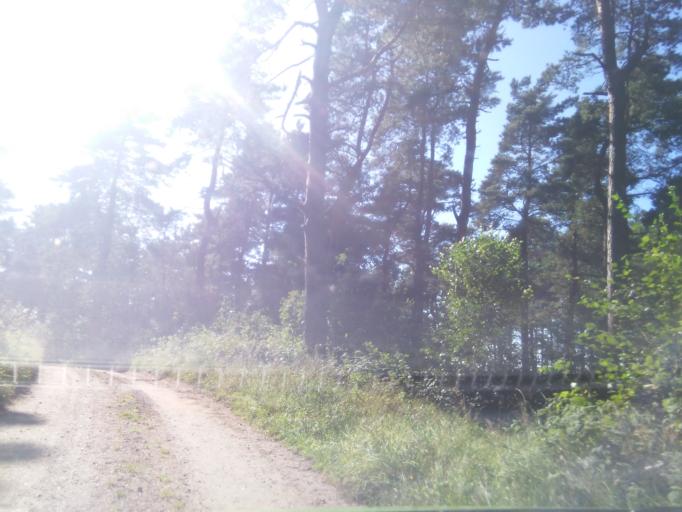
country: DK
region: Central Jutland
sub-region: Syddjurs Kommune
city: Ronde
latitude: 56.2059
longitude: 10.5201
